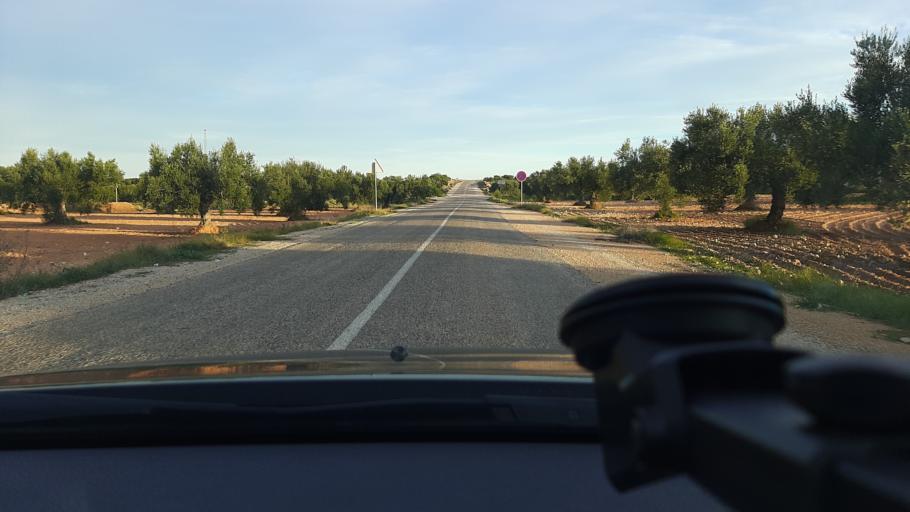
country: TN
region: Safaqis
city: Sfax
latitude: 34.9567
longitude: 10.5437
